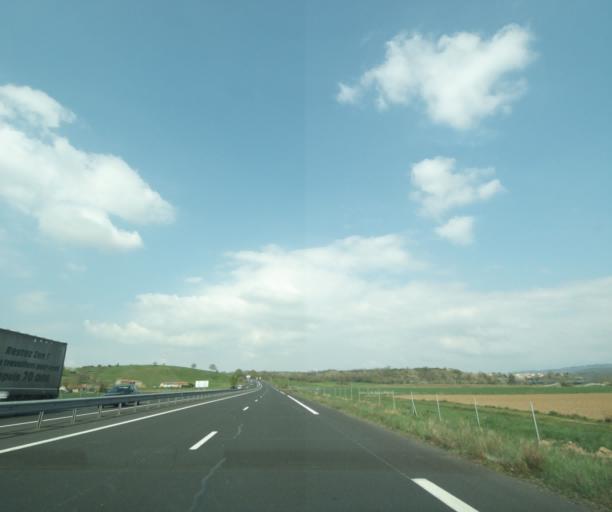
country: FR
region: Auvergne
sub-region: Departement de la Haute-Loire
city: Lempdes-sur-Allagnon
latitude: 45.4046
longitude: 3.2741
